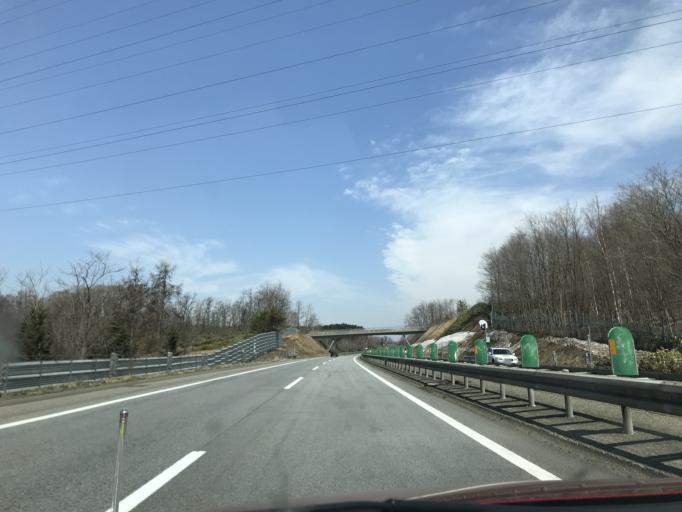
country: JP
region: Hokkaido
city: Bibai
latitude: 43.2554
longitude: 141.8327
